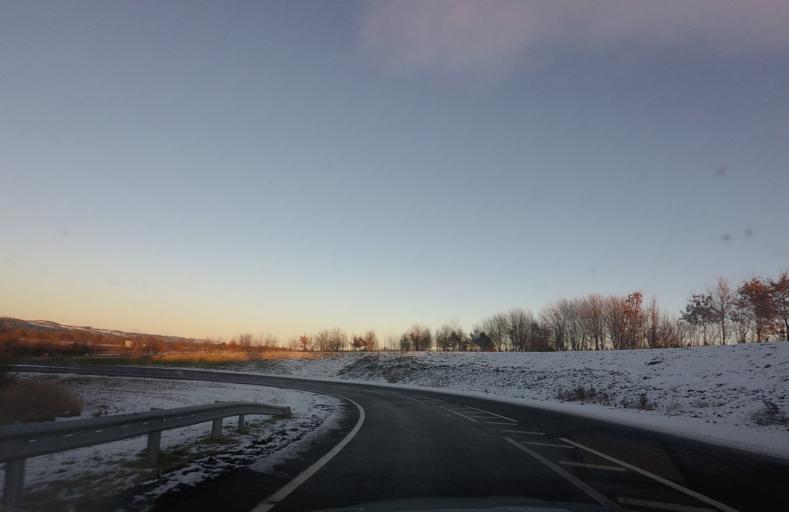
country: GB
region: Scotland
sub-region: Perth and Kinross
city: Errol
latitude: 56.3962
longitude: -3.2678
